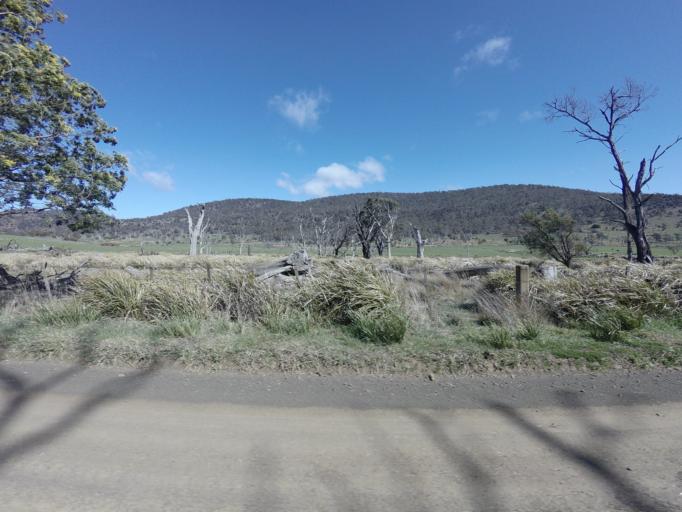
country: AU
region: Tasmania
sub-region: Northern Midlands
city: Evandale
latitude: -41.9369
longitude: 147.4208
